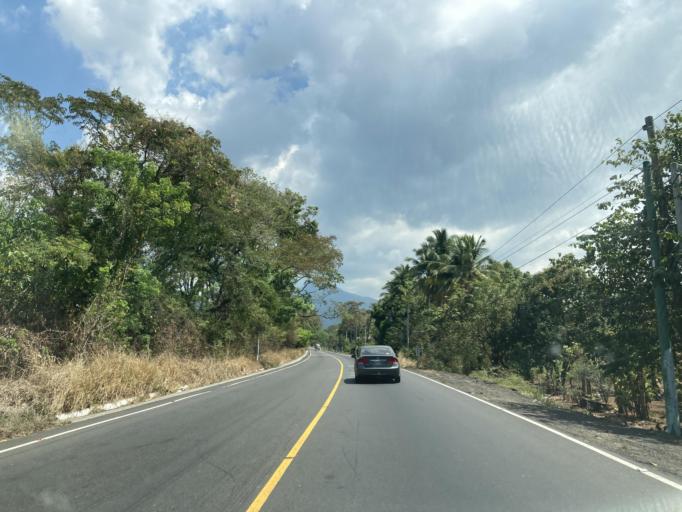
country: GT
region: Santa Rosa
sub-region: Municipio de Taxisco
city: Taxisco
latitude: 14.0986
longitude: -90.5383
